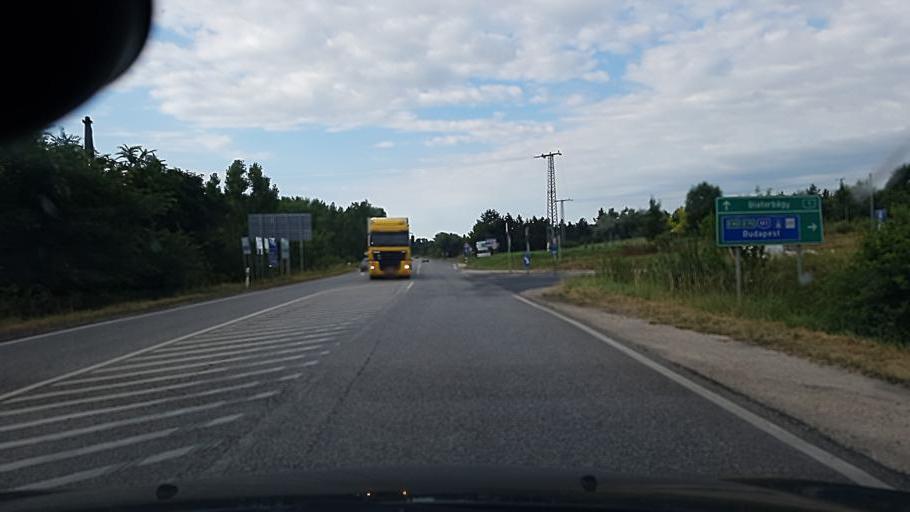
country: HU
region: Pest
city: Zsambek
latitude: 47.5063
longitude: 18.7599
